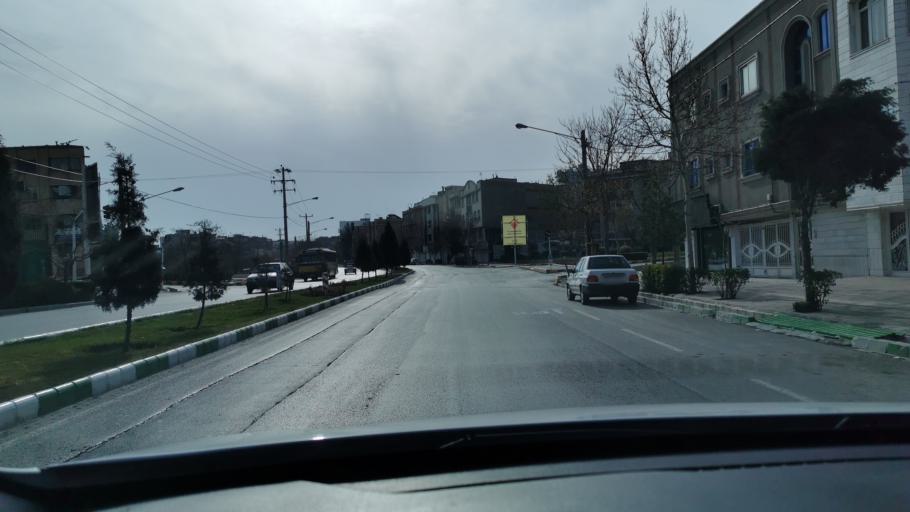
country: IR
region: Razavi Khorasan
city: Mashhad
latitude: 36.3144
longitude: 59.5113
